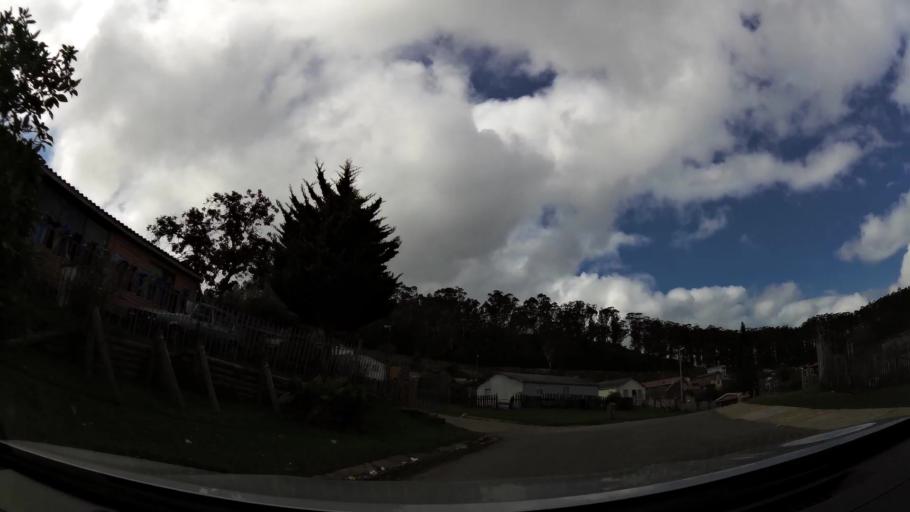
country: ZA
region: Western Cape
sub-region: Eden District Municipality
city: Knysna
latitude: -34.0512
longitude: 23.1049
